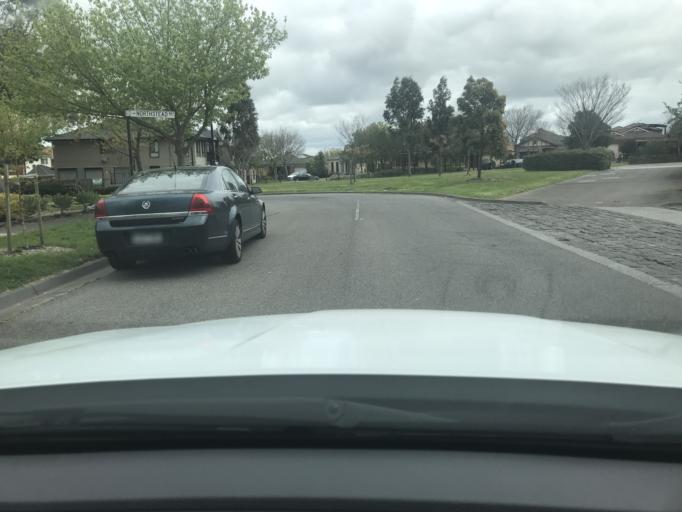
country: AU
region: Victoria
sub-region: Hume
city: Craigieburn
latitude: -37.5752
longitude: 144.9289
